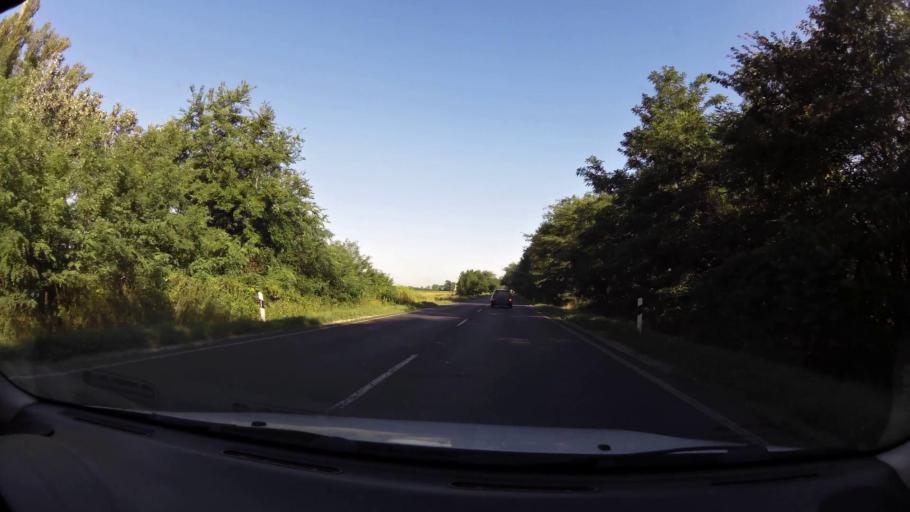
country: HU
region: Pest
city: Pilis
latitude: 47.2975
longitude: 19.5239
